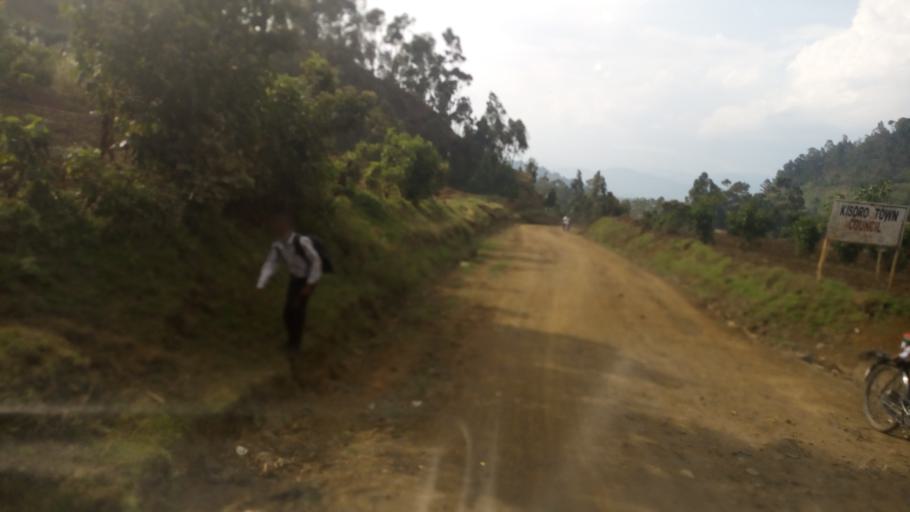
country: UG
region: Western Region
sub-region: Kisoro District
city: Kisoro
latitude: -1.2997
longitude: 29.7022
